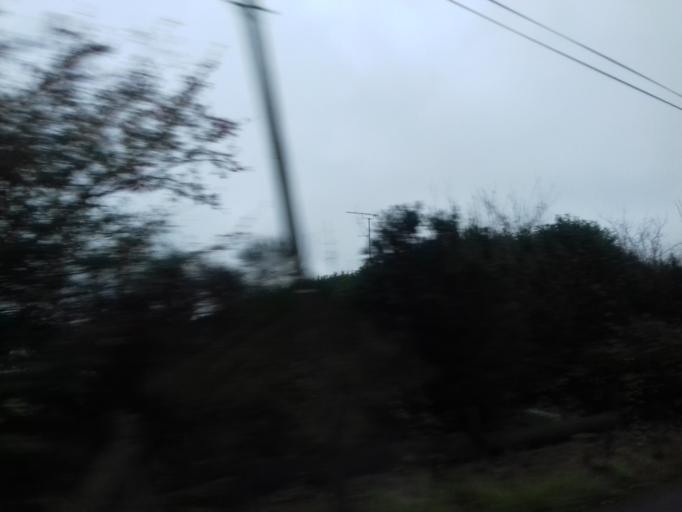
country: IE
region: Ulster
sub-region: County Monaghan
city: Castleblayney
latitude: 54.0760
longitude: -6.6829
